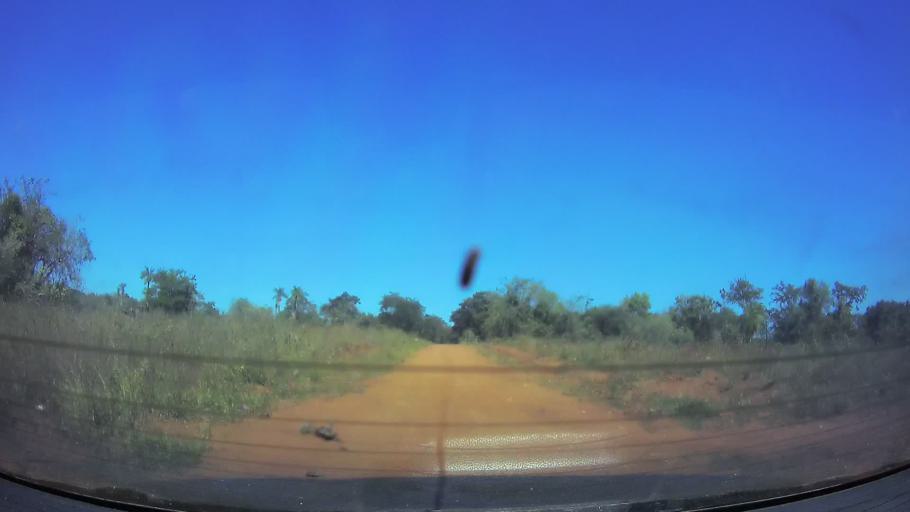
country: PY
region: Central
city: Limpio
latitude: -25.2398
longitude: -57.4525
